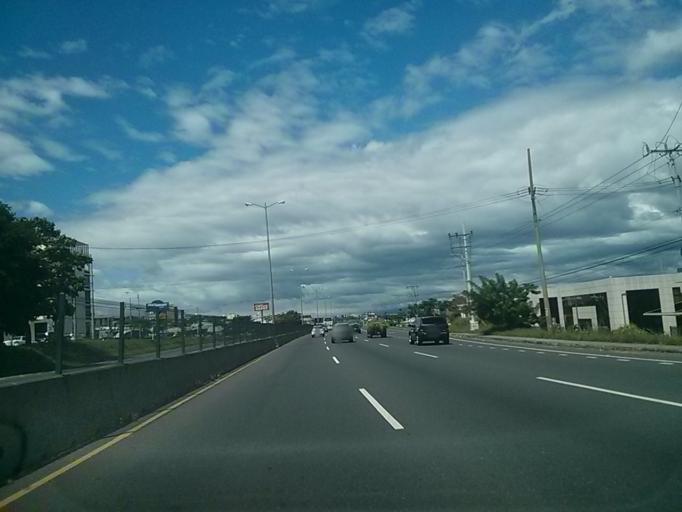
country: CR
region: San Jose
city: San Rafael
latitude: 9.9408
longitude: -84.1438
